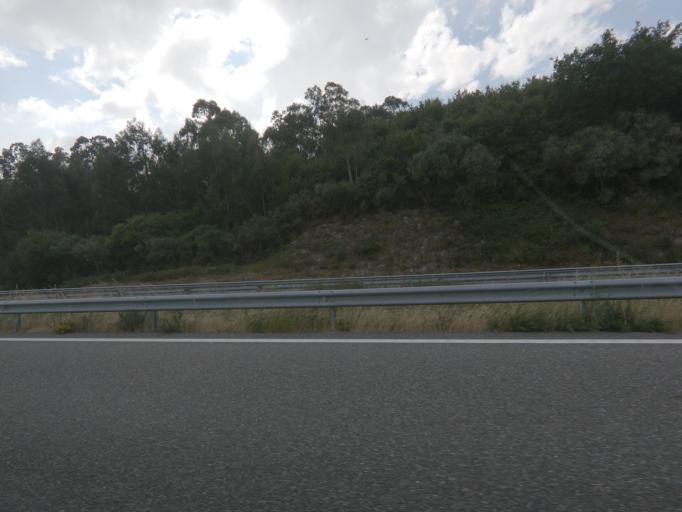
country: ES
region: Galicia
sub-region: Provincia de Ourense
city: Melon
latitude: 42.2377
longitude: -8.2293
